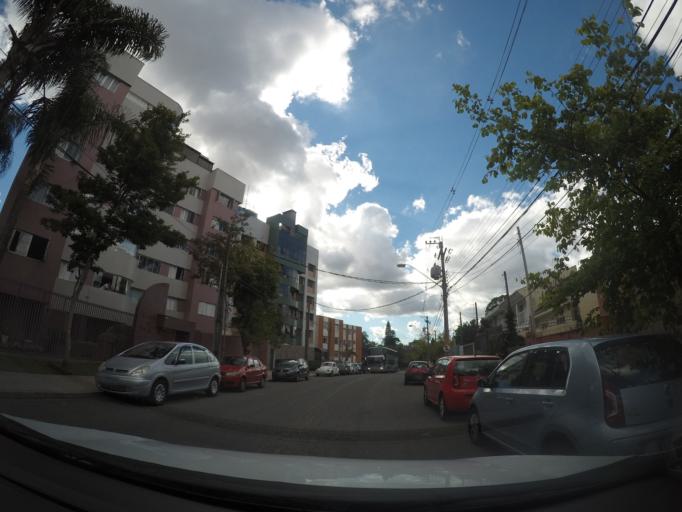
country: BR
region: Parana
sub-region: Curitiba
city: Curitiba
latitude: -25.4080
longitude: -49.2667
